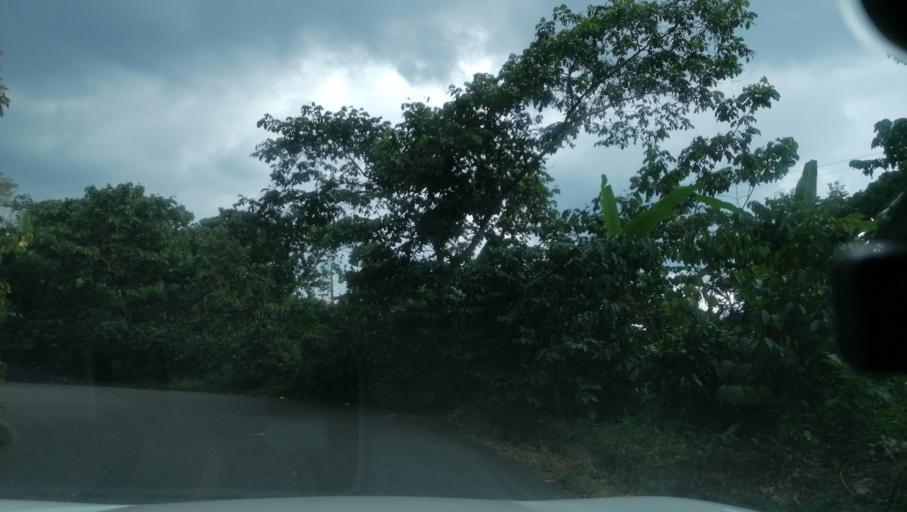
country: MX
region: Chiapas
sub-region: Cacahoatan
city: Benito Juarez
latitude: 15.0723
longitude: -92.1923
